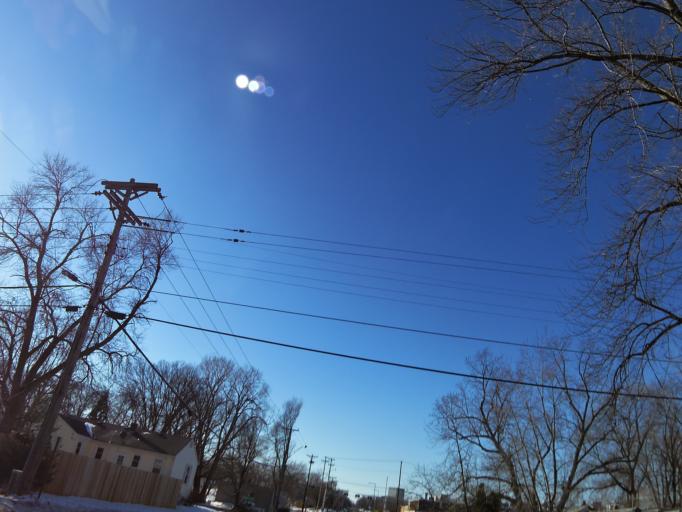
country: US
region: Minnesota
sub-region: Hennepin County
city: Bloomington
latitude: 44.8553
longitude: -93.2813
